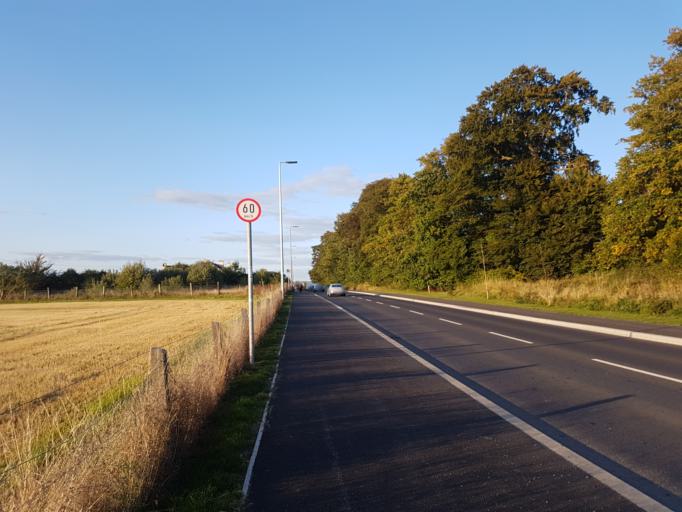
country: IE
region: Leinster
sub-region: Kilkenny
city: Kilkenny
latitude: 52.6354
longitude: -7.2729
